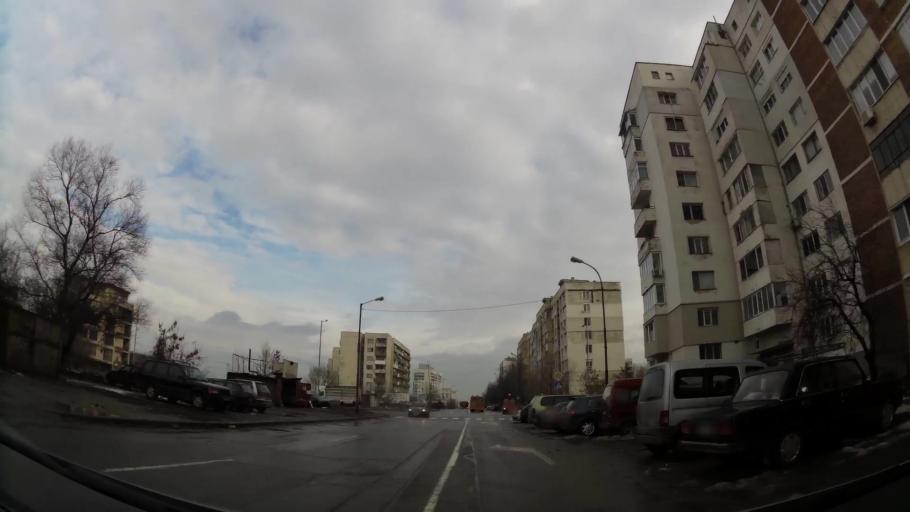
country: BG
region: Sofiya
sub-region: Obshtina Bozhurishte
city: Bozhurishte
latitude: 42.7184
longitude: 23.2386
